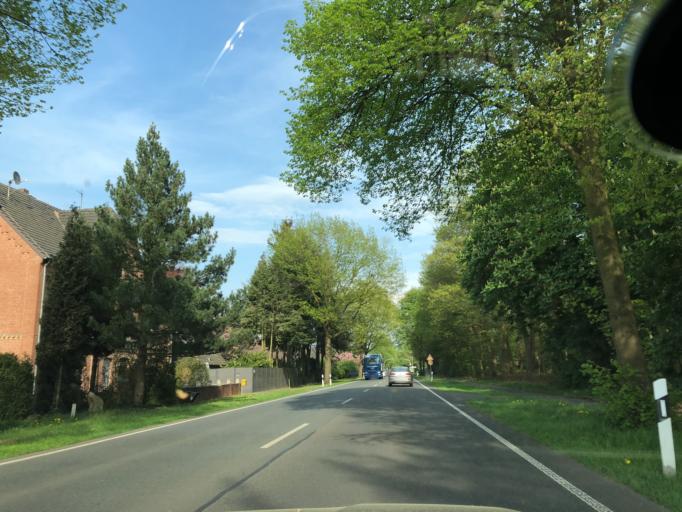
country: DE
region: North Rhine-Westphalia
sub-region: Regierungsbezirk Dusseldorf
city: Wesel
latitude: 51.6634
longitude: 6.6802
